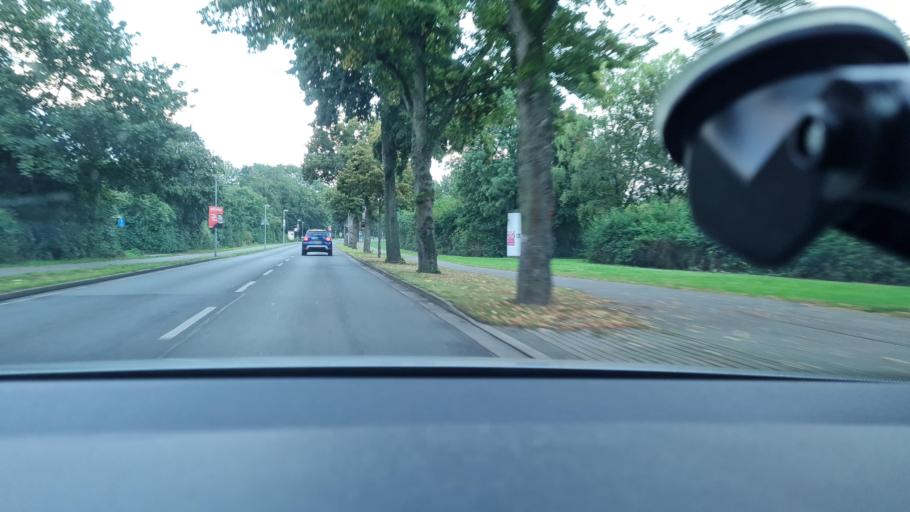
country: DE
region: North Rhine-Westphalia
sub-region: Regierungsbezirk Dusseldorf
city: Moers
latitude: 51.4820
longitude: 6.6203
